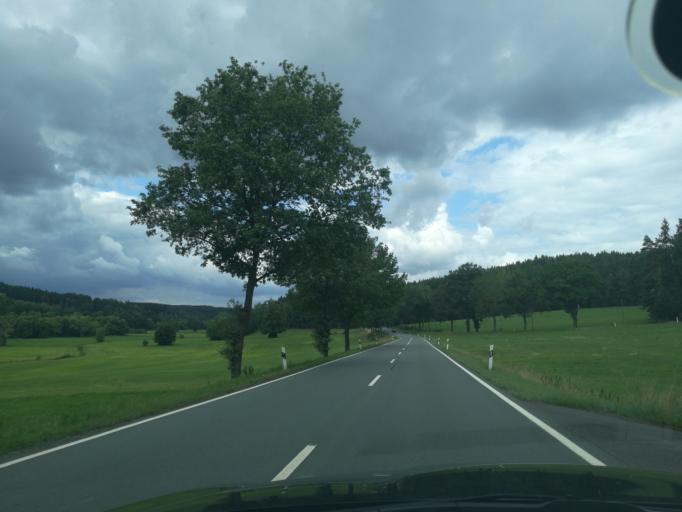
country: DE
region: Saxony
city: Eichigt
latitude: 50.3788
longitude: 12.2037
